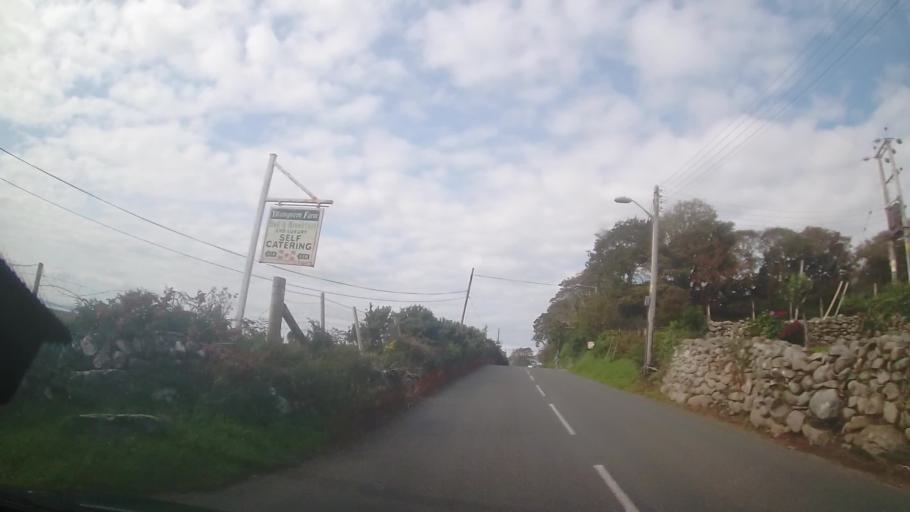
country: GB
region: Wales
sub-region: Gwynedd
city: Llanbedr
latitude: 52.7969
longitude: -4.1005
